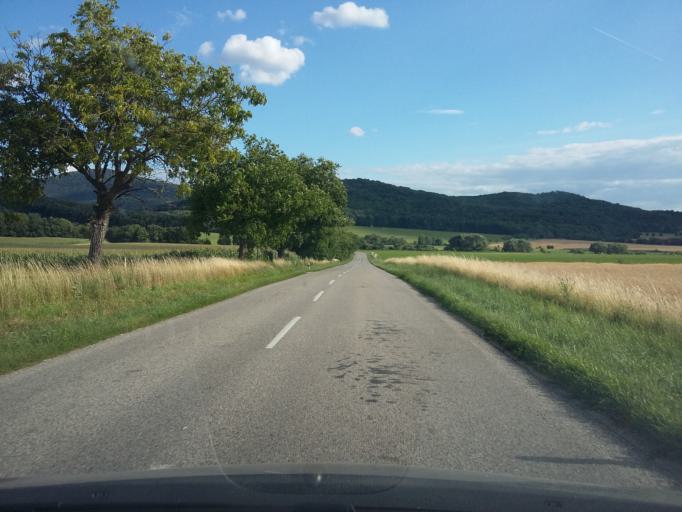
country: SK
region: Trnavsky
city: Smolenice
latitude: 48.5516
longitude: 17.3496
